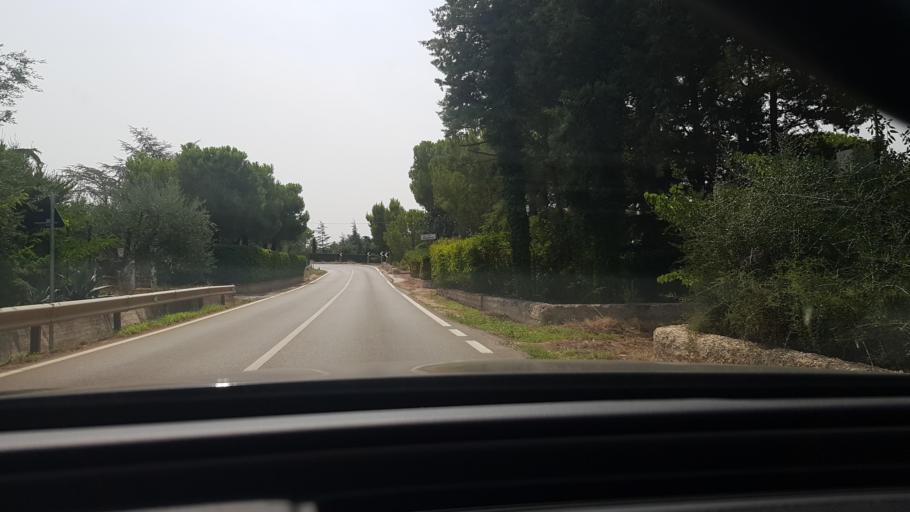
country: IT
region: Apulia
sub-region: Provincia di Barletta - Andria - Trani
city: Andria
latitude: 41.1382
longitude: 16.2894
